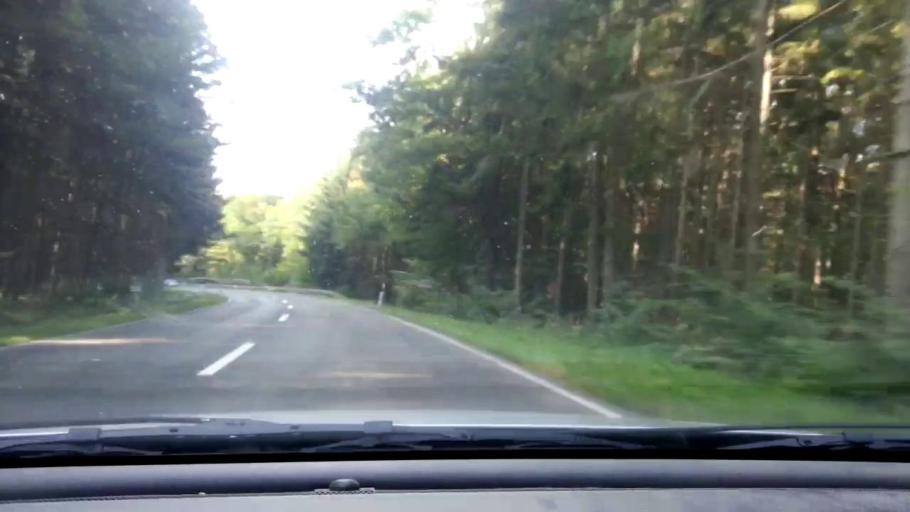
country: DE
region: Bavaria
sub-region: Upper Franconia
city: Zapfendorf
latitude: 50.0091
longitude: 10.9486
